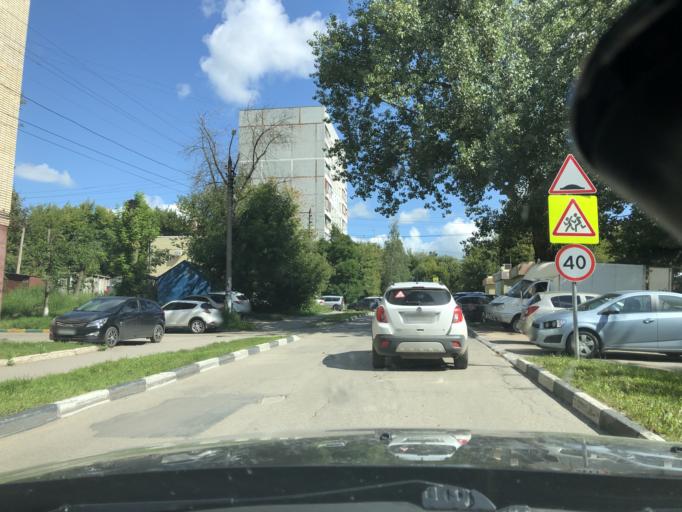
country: RU
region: Tula
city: Tula
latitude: 54.2127
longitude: 37.6256
